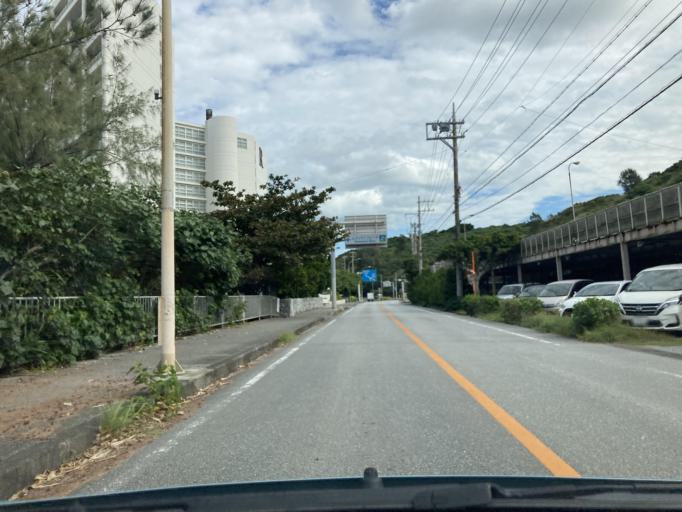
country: JP
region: Okinawa
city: Ishikawa
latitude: 26.4348
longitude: 127.7870
